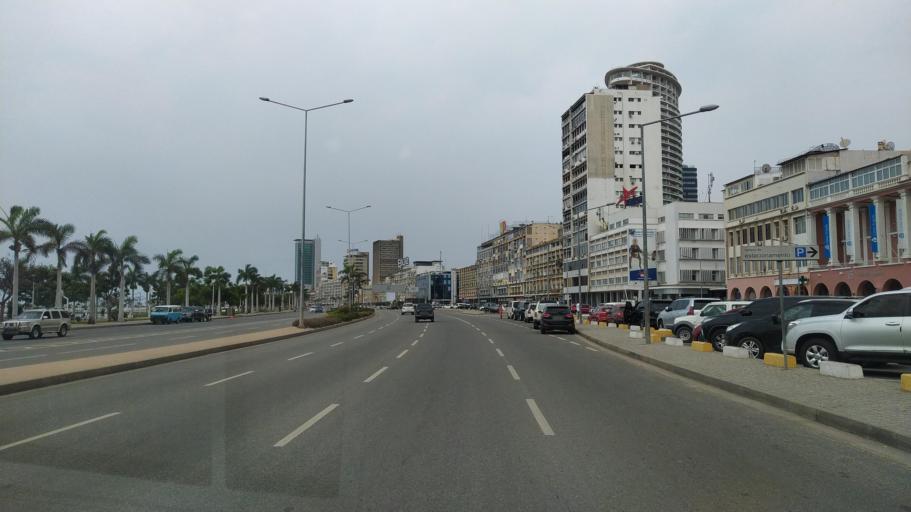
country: AO
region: Luanda
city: Luanda
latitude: -8.8094
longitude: 13.2362
